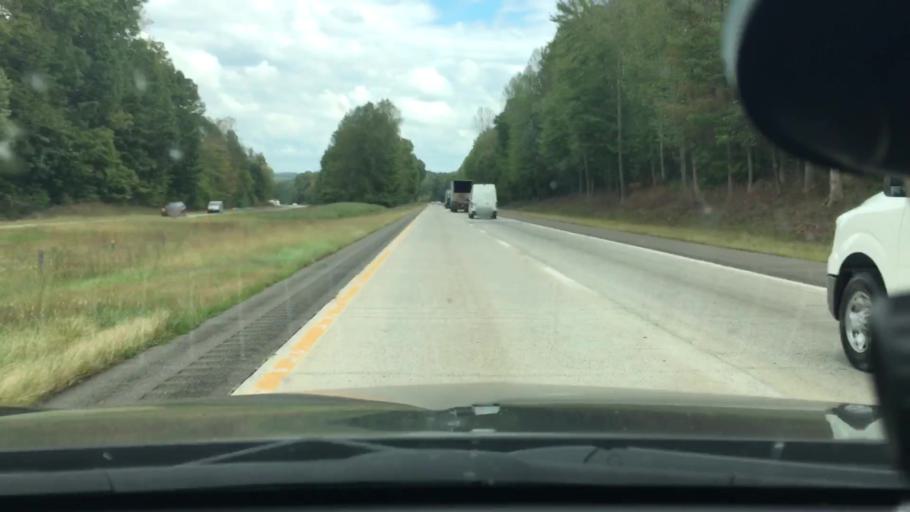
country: US
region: North Carolina
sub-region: Davie County
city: Mocksville
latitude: 35.8884
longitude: -80.6640
